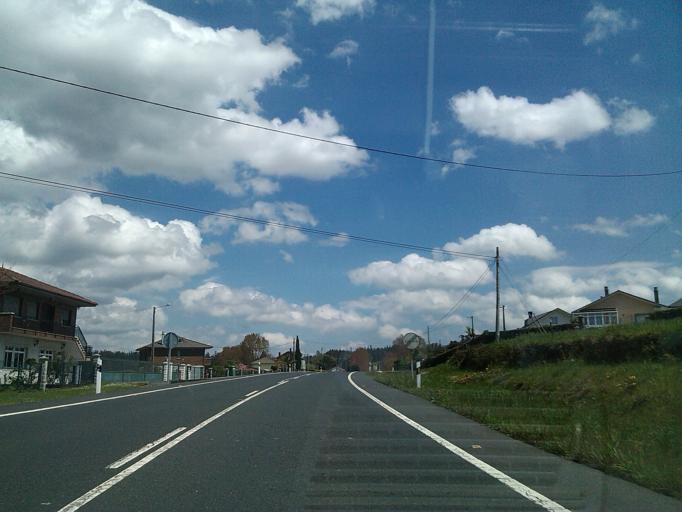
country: ES
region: Galicia
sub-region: Provincia da Coruna
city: Santiso
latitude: 42.9184
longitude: -8.0707
